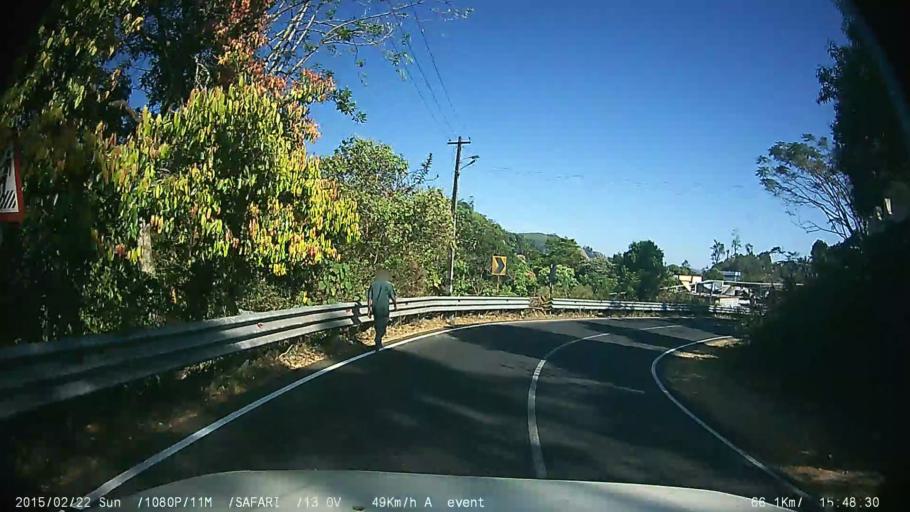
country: IN
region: Kerala
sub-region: Kottayam
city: Erattupetta
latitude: 9.5733
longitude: 76.9932
